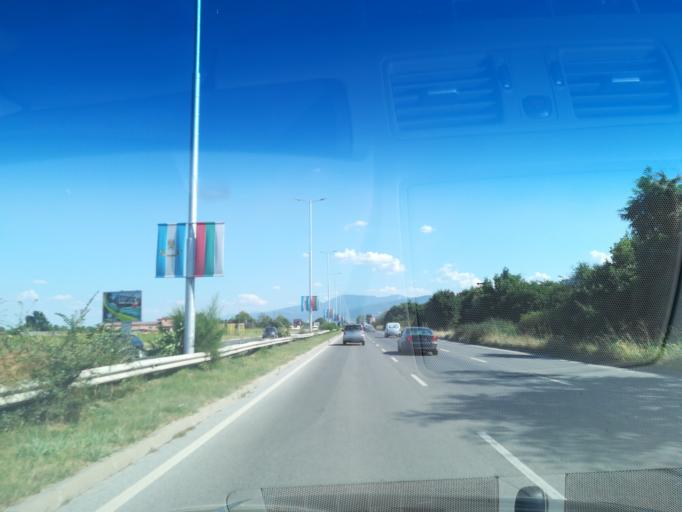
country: BG
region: Plovdiv
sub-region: Obshtina Plovdiv
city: Plovdiv
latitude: 42.1064
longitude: 24.7832
